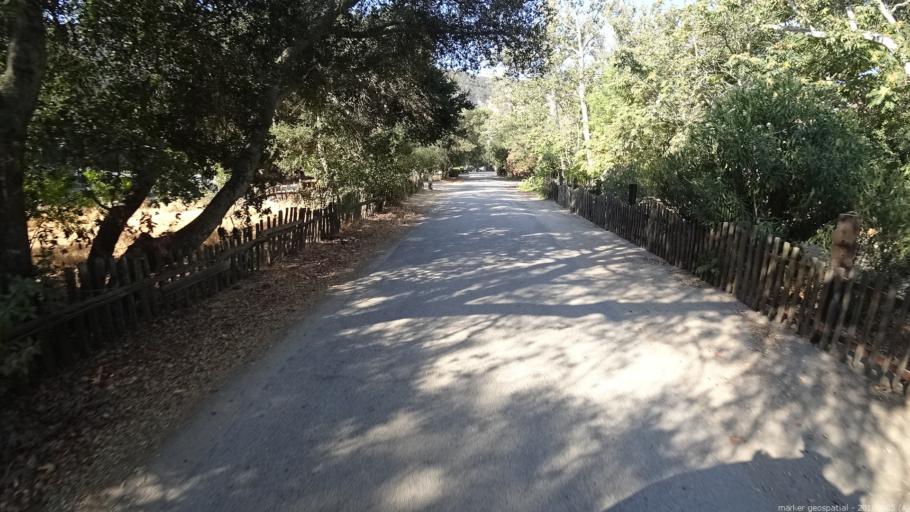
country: US
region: California
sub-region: Monterey County
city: Greenfield
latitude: 36.2646
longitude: -121.3928
